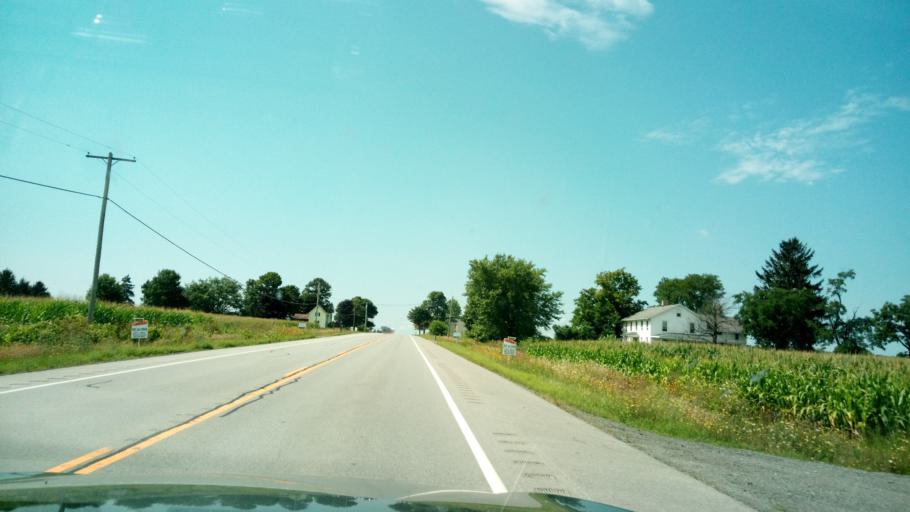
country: US
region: New York
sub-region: Wyoming County
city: Perry
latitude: 42.8326
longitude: -77.9488
